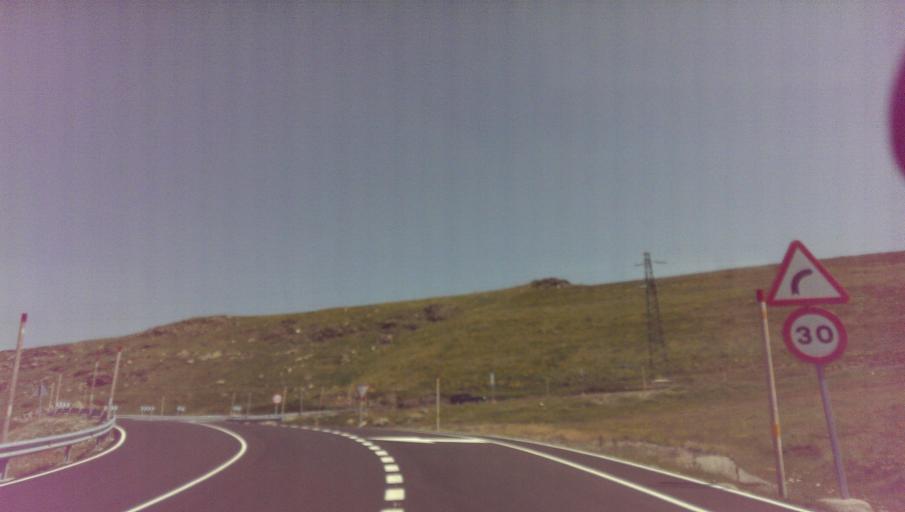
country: AD
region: Encamp
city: Pas de la Casa
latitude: 42.5416
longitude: 1.7162
